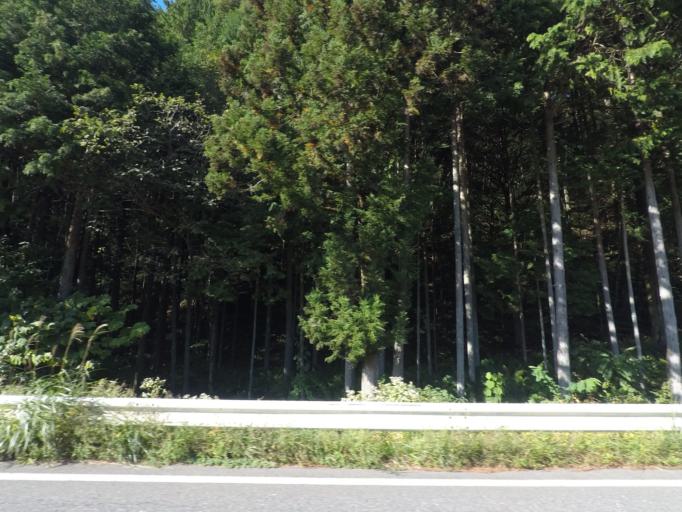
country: JP
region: Nagano
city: Ina
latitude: 35.9578
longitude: 137.7678
